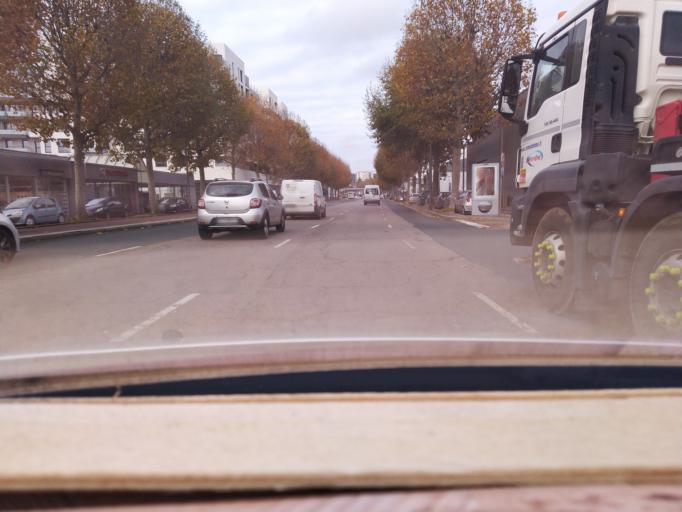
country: FR
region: Haute-Normandie
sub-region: Departement de la Seine-Maritime
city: Mont-Saint-Aignan
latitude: 49.4468
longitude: 1.0699
